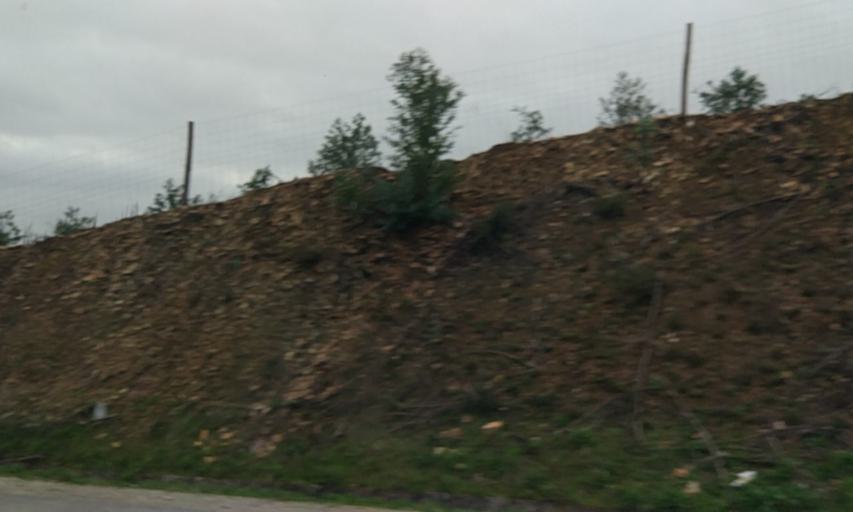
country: PT
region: Viseu
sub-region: Mortagua
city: Mortagua
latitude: 40.3543
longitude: -8.1935
